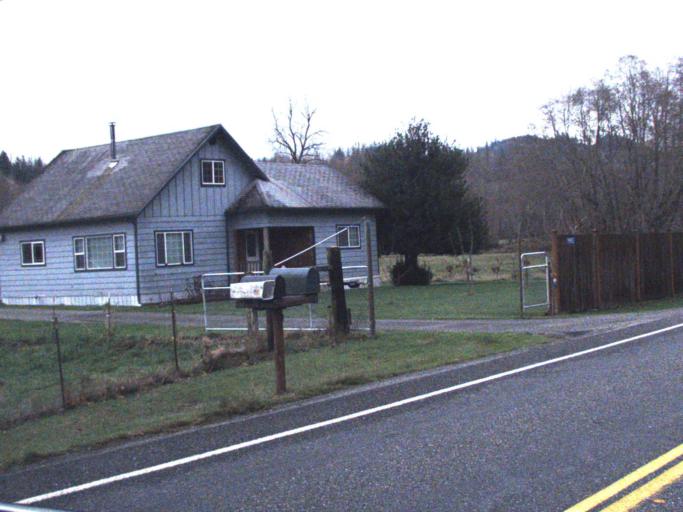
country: US
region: Washington
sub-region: Skagit County
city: Big Lake
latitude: 48.3570
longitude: -122.2036
